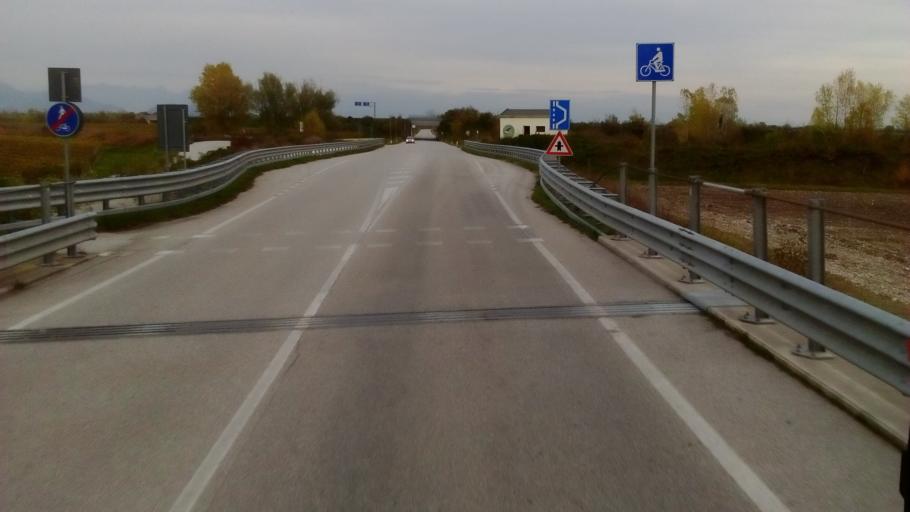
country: IT
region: Friuli Venezia Giulia
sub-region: Provincia di Pordenone
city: Vivaro
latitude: 46.0926
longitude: 12.8168
